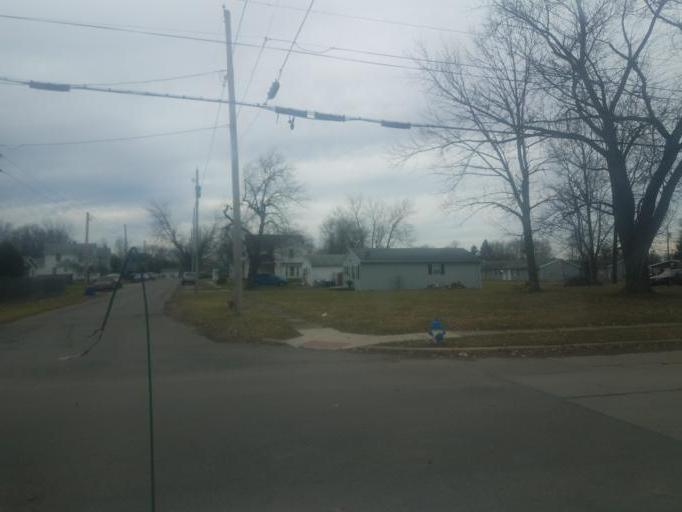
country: US
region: Ohio
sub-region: Marion County
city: Marion
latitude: 40.5981
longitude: -83.1181
